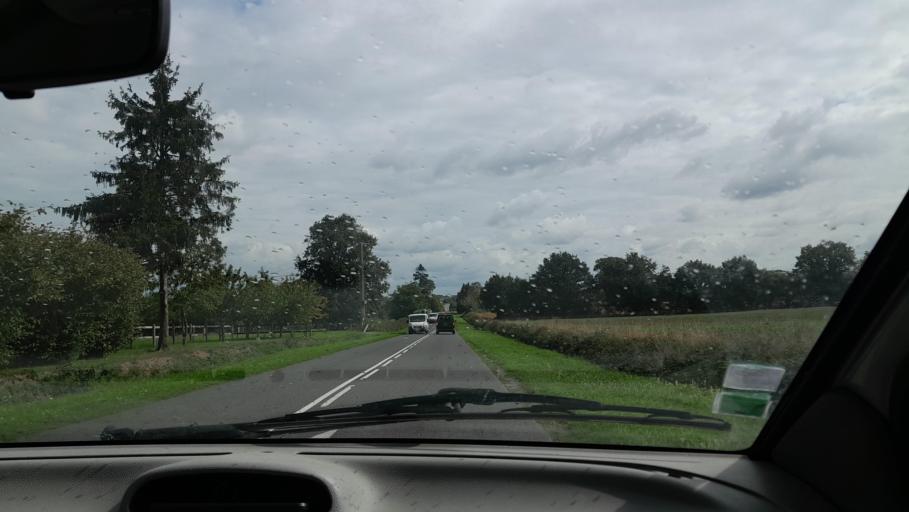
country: FR
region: Pays de la Loire
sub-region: Departement de la Mayenne
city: Cosse-le-Vivien
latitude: 47.9552
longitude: -0.9509
